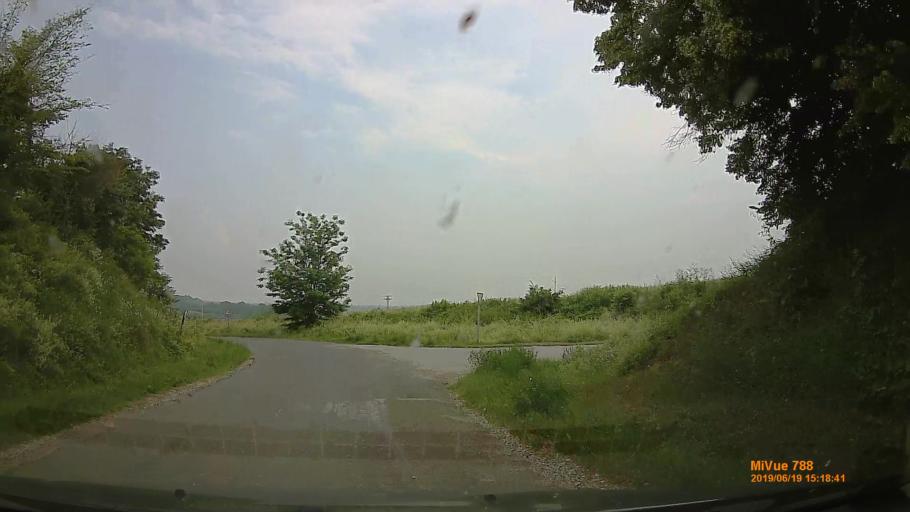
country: HU
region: Baranya
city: Szigetvar
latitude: 46.0757
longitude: 17.8577
